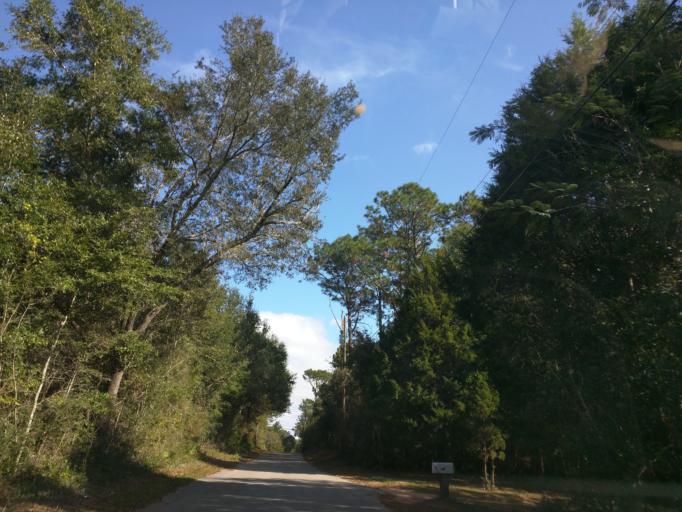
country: US
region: Florida
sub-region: Escambia County
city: Cantonment
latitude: 30.5492
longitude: -87.4156
